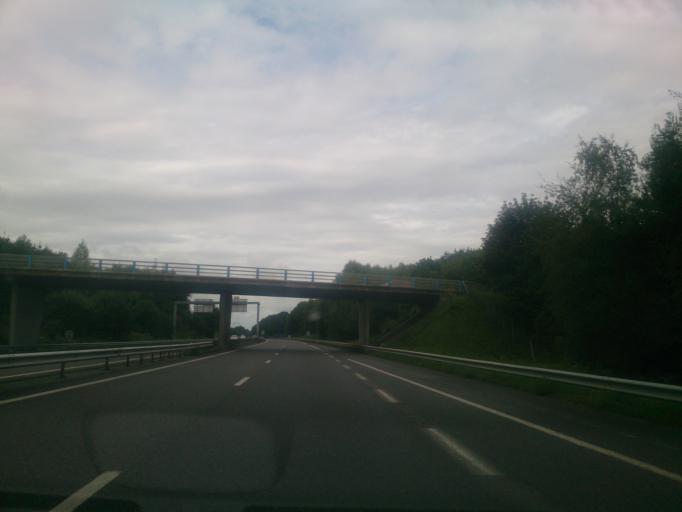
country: FR
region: Midi-Pyrenees
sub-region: Departement des Hautes-Pyrenees
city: La Barthe-de-Neste
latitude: 43.1006
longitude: 0.3887
